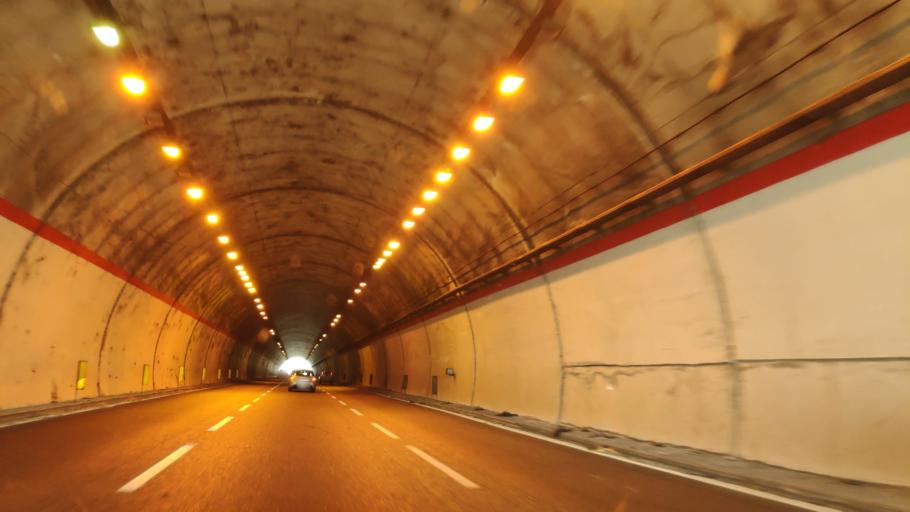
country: IT
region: Campania
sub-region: Provincia di Salerno
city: Quadrivio
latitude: 40.6105
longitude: 15.1344
